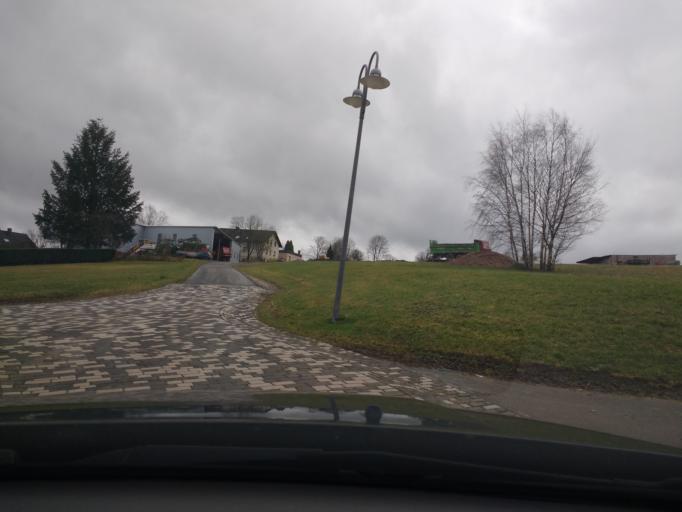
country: DE
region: Rheinland-Pfalz
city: Schillingen
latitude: 49.6366
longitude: 6.7831
